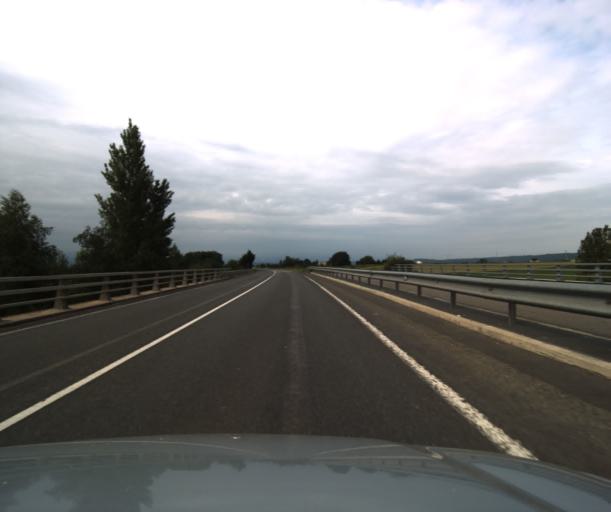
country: FR
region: Midi-Pyrenees
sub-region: Departement des Hautes-Pyrenees
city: Juillan
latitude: 43.2190
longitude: 0.0171
